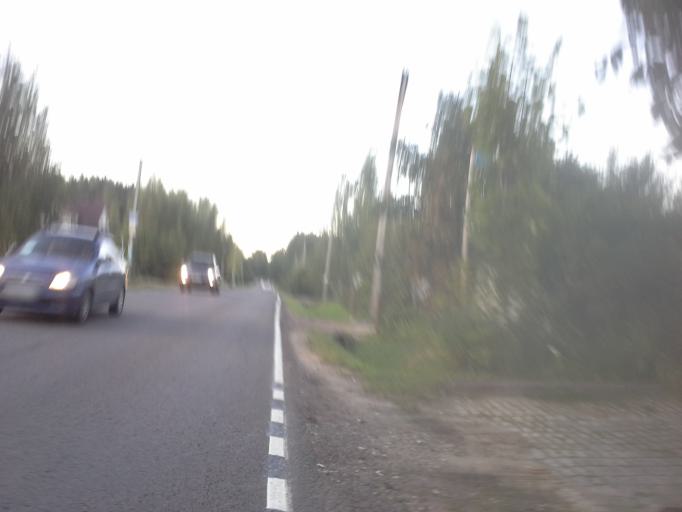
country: RU
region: Moskovskaya
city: Selyatino
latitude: 55.5069
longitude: 36.9340
